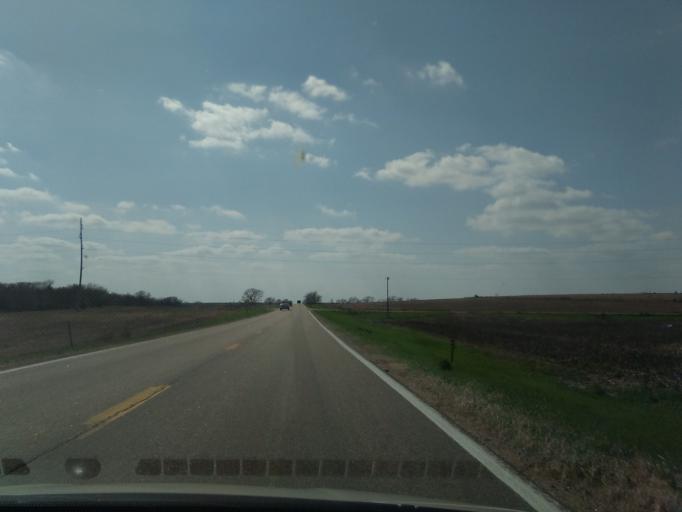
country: US
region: Nebraska
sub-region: Thayer County
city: Hebron
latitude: 40.1472
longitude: -97.6307
